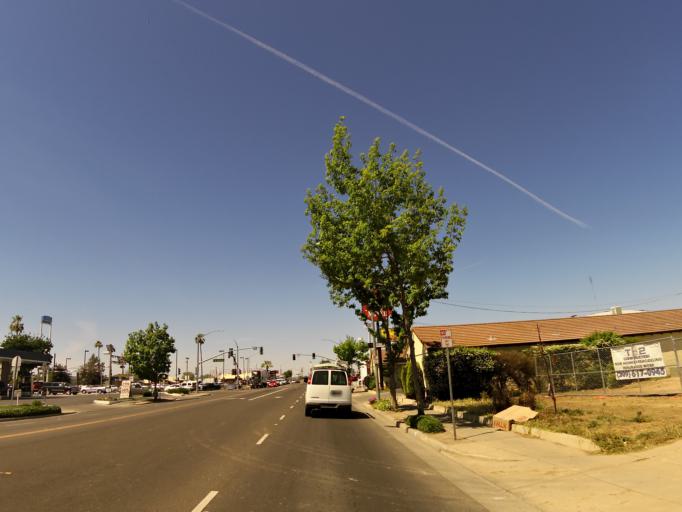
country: US
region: California
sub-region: Merced County
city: Merced
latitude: 37.3057
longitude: -120.4980
